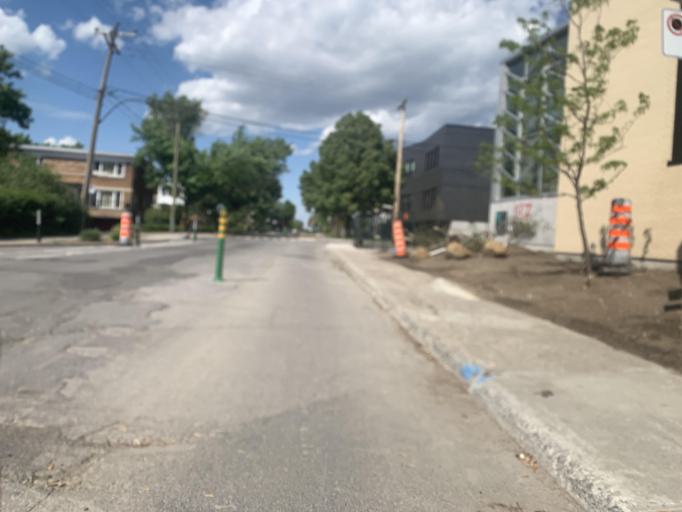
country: CA
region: Quebec
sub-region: Montreal
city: Saint-Leonard
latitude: 45.5523
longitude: -73.5838
